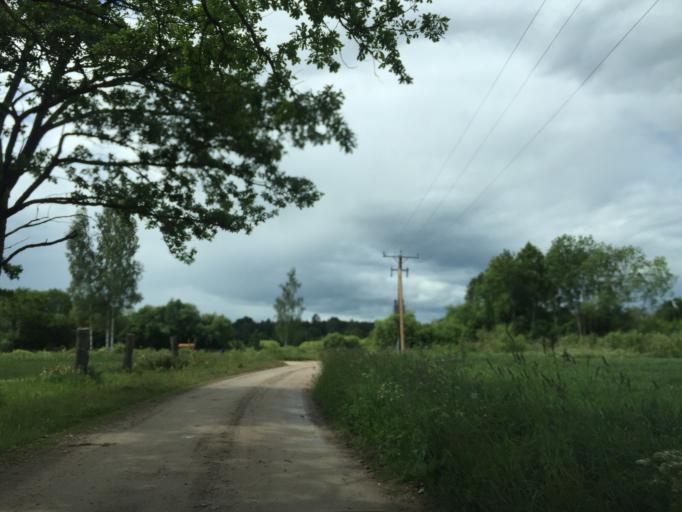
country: LV
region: Lecava
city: Iecava
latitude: 56.5611
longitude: 24.1193
